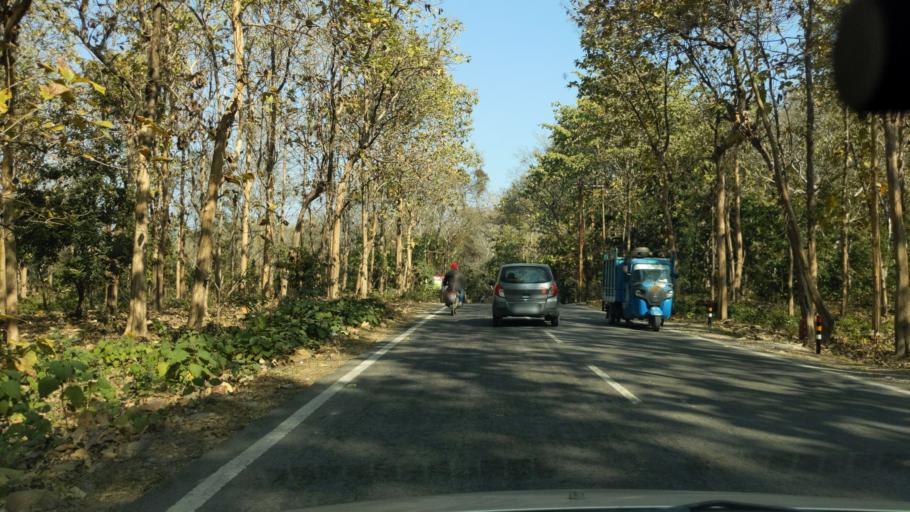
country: IN
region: Uttarakhand
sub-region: Naini Tal
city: Ramnagar
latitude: 29.3842
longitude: 79.1426
